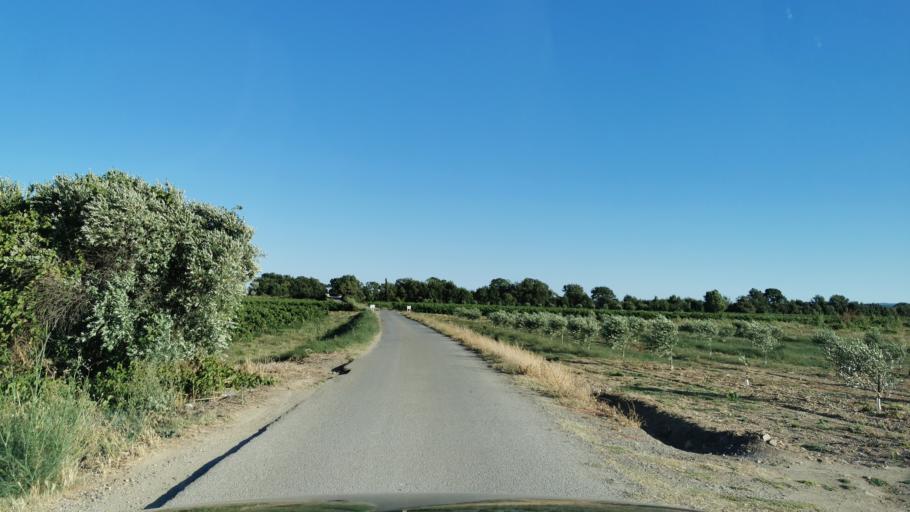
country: FR
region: Languedoc-Roussillon
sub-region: Departement de l'Aude
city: Ouveillan
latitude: 43.2639
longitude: 2.9847
